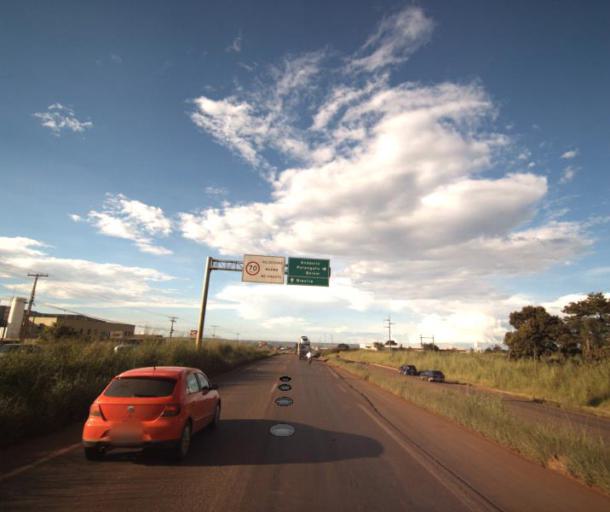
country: BR
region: Goias
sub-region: Anapolis
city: Anapolis
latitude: -16.3584
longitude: -48.9316
